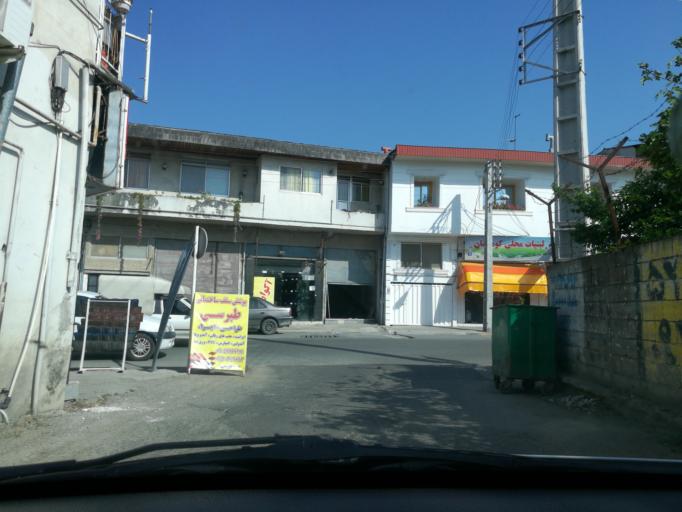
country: IR
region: Mazandaran
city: Chalus
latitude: 36.6577
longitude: 51.4256
